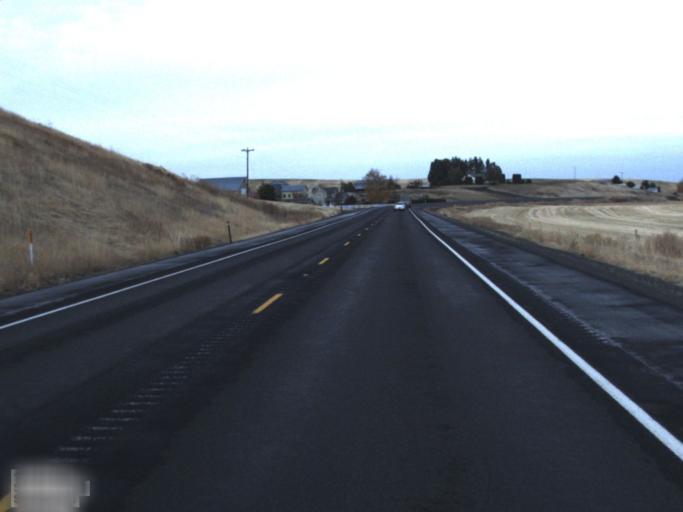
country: US
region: Washington
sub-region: Asotin County
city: Clarkston
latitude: 46.5498
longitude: -117.0985
